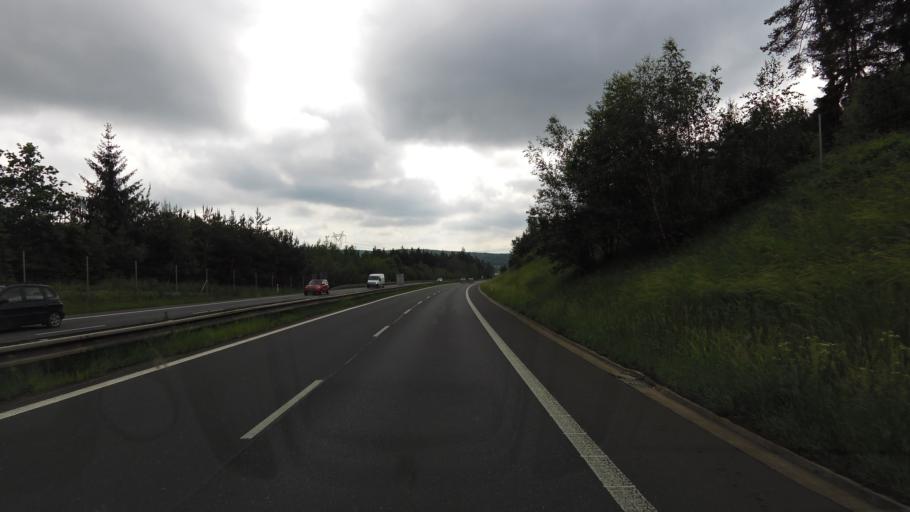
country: CZ
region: Plzensky
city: Dysina
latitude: 49.7448
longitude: 13.4940
